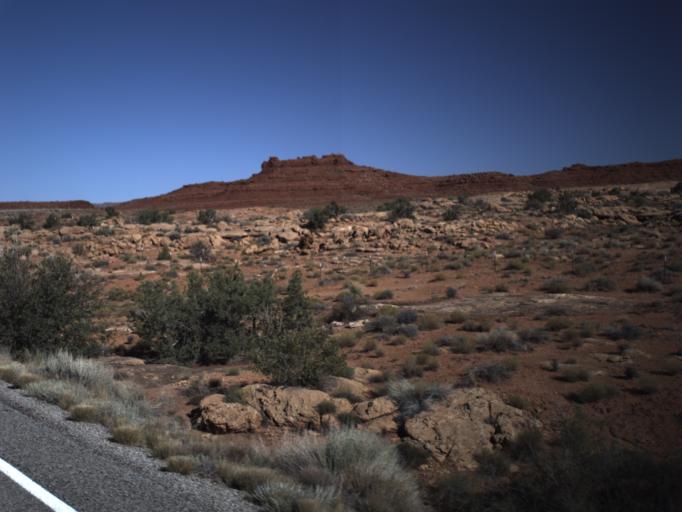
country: US
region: Utah
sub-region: San Juan County
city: Blanding
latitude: 37.8215
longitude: -110.3555
